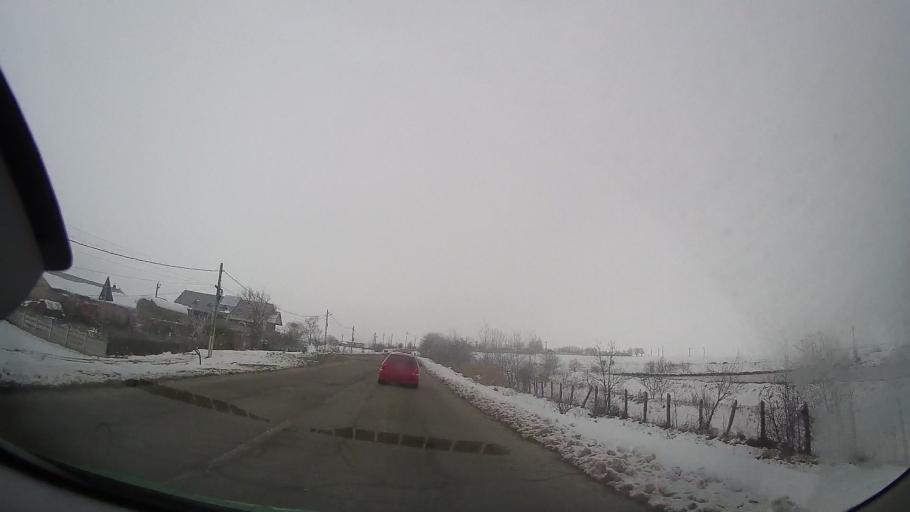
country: RO
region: Vaslui
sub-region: Comuna Negresti
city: Negresti
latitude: 46.8360
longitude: 27.4469
